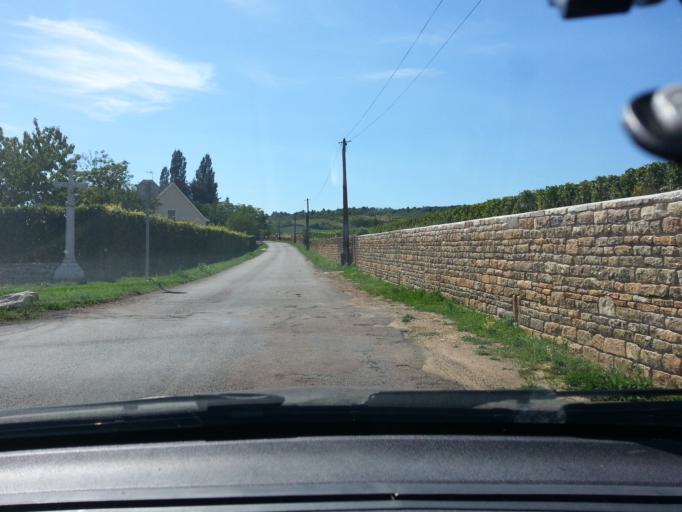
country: FR
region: Bourgogne
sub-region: Departement de Saone-et-Loire
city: Givry
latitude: 46.7775
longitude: 4.7269
